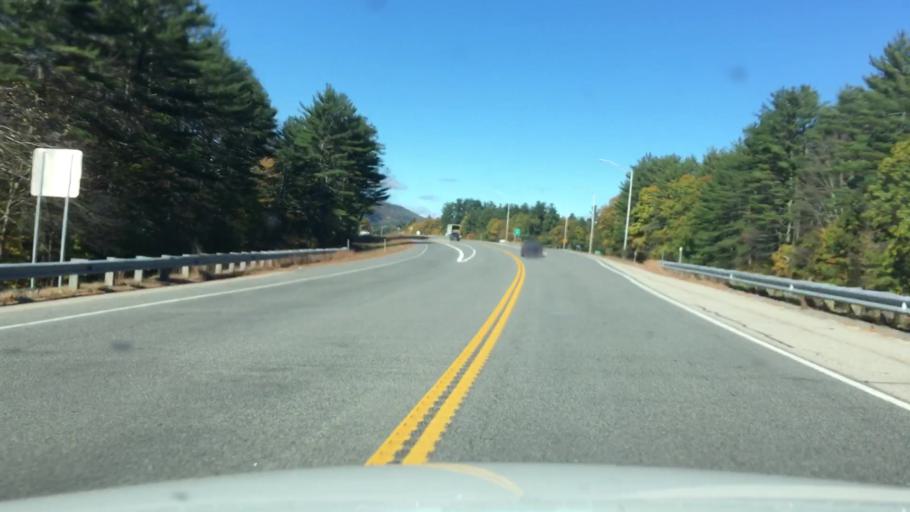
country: US
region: New Hampshire
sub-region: Carroll County
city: Ossipee
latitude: 43.7535
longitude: -71.1371
